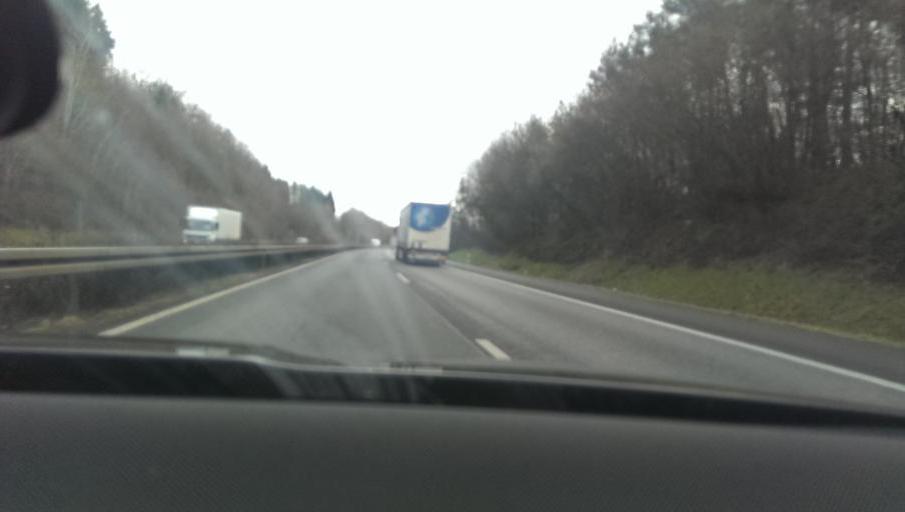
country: DE
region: Hesse
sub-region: Regierungsbezirk Darmstadt
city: Wachtersbach
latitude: 50.2405
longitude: 9.2986
